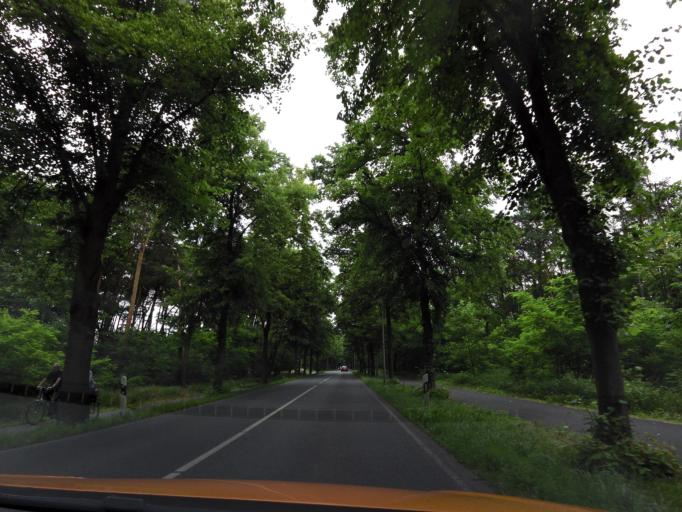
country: DE
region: Brandenburg
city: Zossen
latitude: 52.1760
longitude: 13.4686
